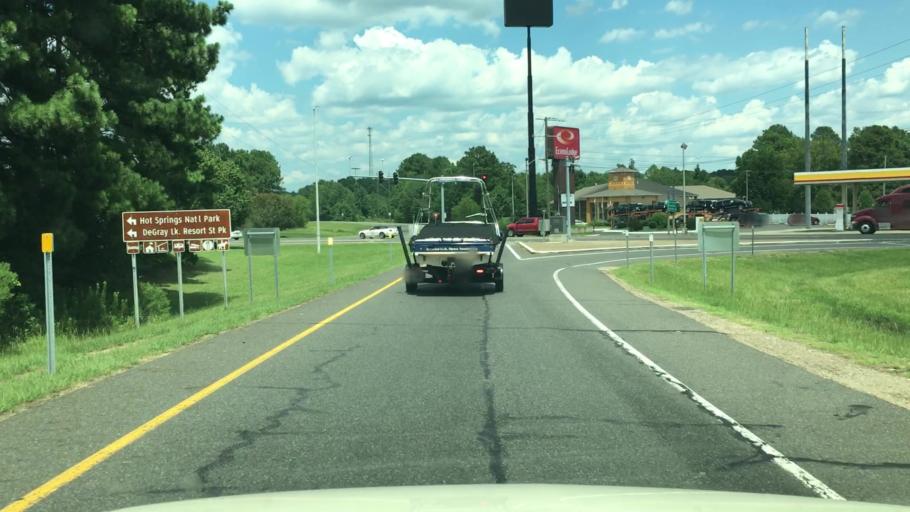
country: US
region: Arkansas
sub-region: Clark County
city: Arkadelphia
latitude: 34.1834
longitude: -93.0715
